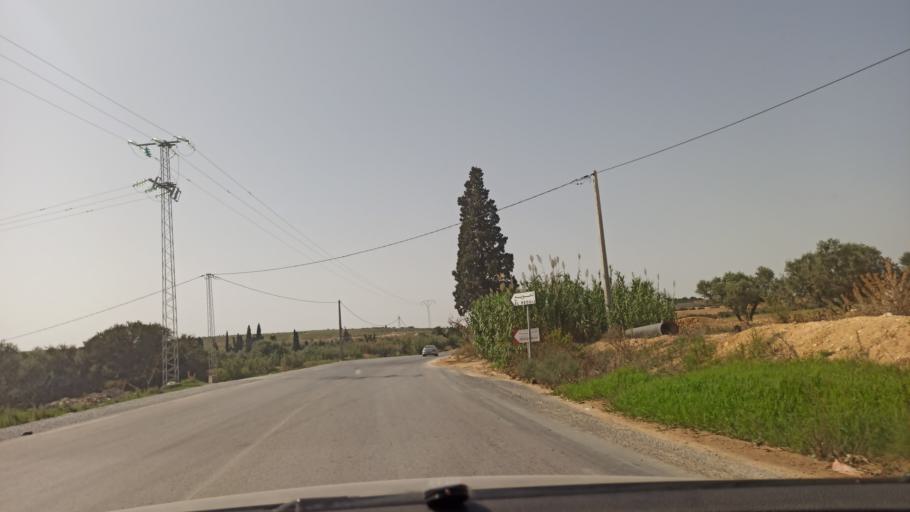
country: TN
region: Manouba
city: Manouba
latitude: 36.7466
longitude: 10.0960
